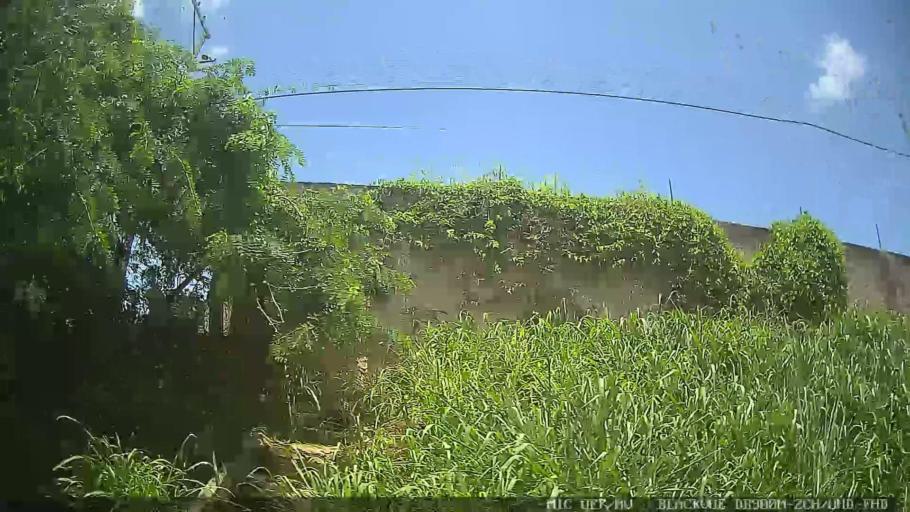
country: BR
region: Sao Paulo
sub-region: Laranjal Paulista
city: Laranjal Paulista
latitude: -23.0355
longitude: -47.8563
